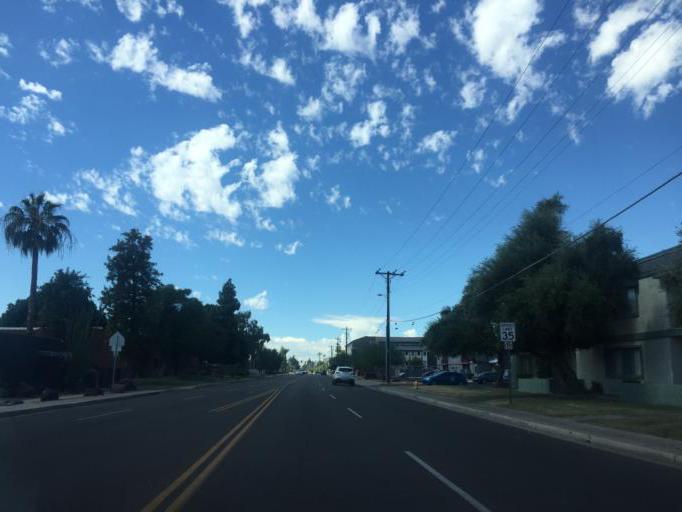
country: US
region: Arizona
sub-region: Maricopa County
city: Phoenix
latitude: 33.5169
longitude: -112.0961
